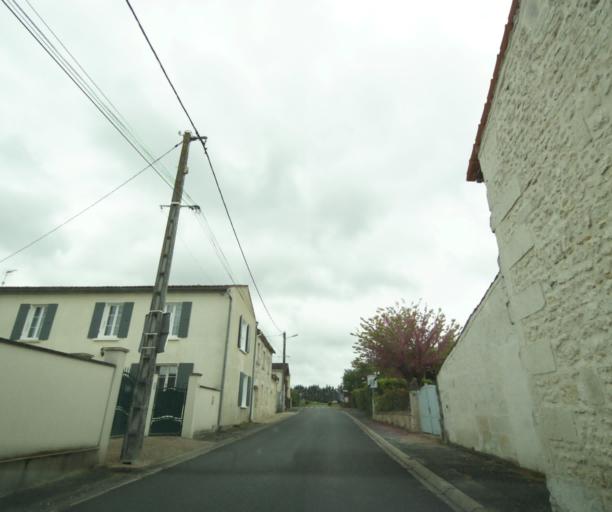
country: FR
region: Poitou-Charentes
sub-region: Departement de la Charente-Maritime
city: Chaniers
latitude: 45.7012
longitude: -0.5492
